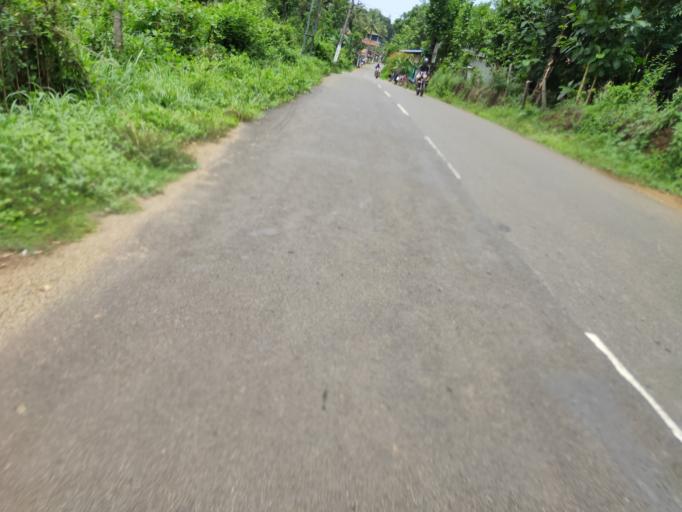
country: IN
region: Kerala
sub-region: Malappuram
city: Manjeri
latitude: 11.2172
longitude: 76.2610
